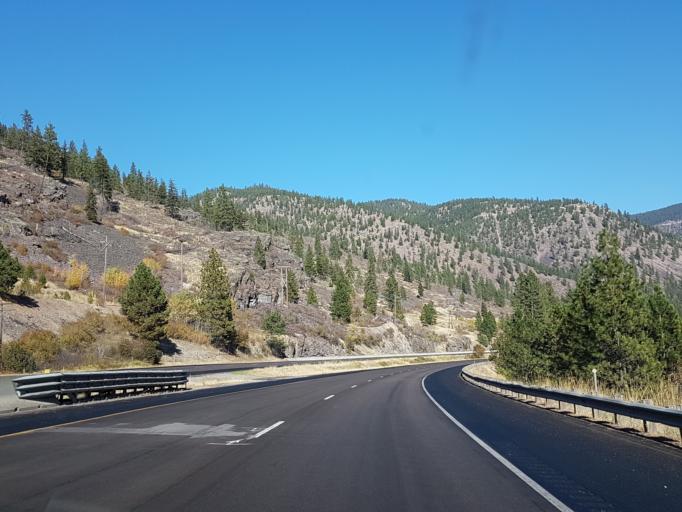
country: US
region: Montana
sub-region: Missoula County
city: Frenchtown
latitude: 47.0182
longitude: -114.5382
